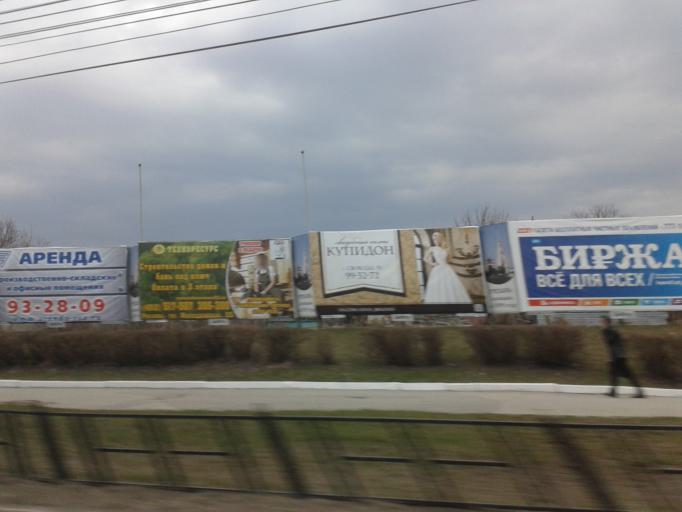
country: RU
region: Rjazan
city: Ryazan'
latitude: 54.6321
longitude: 39.7000
